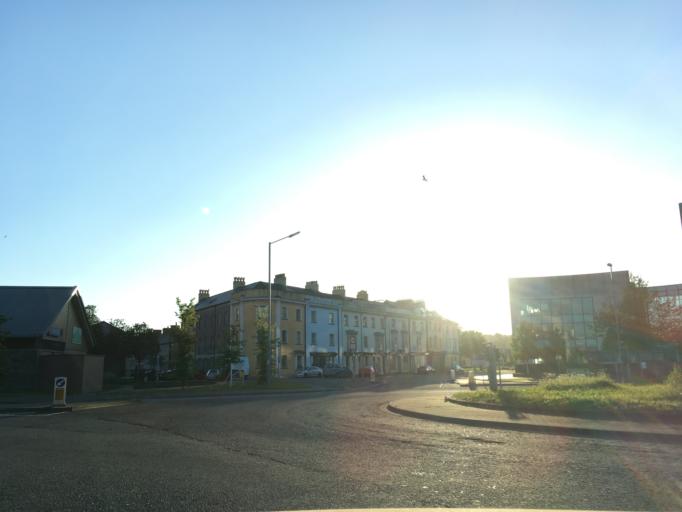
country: GB
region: Wales
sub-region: Newport
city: Newport
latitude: 51.5808
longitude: -2.9848
